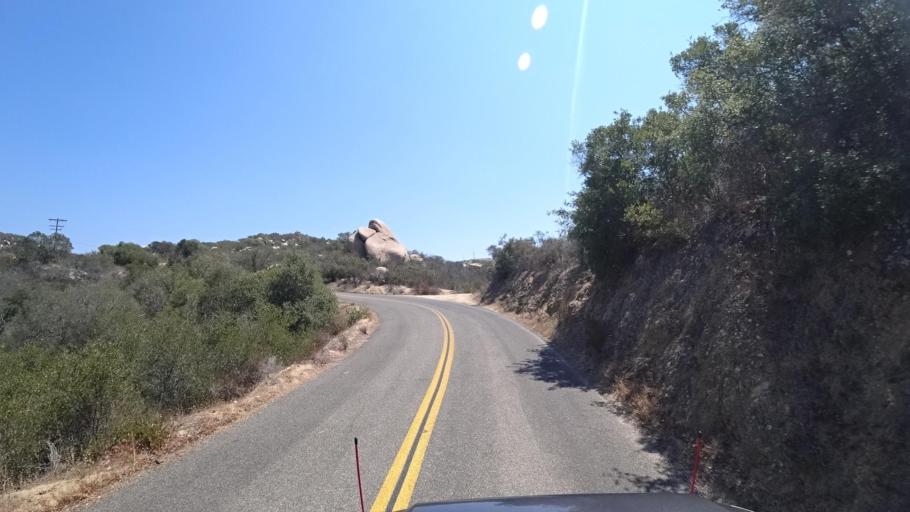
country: US
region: California
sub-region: San Diego County
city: Fallbrook
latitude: 33.4510
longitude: -117.2804
